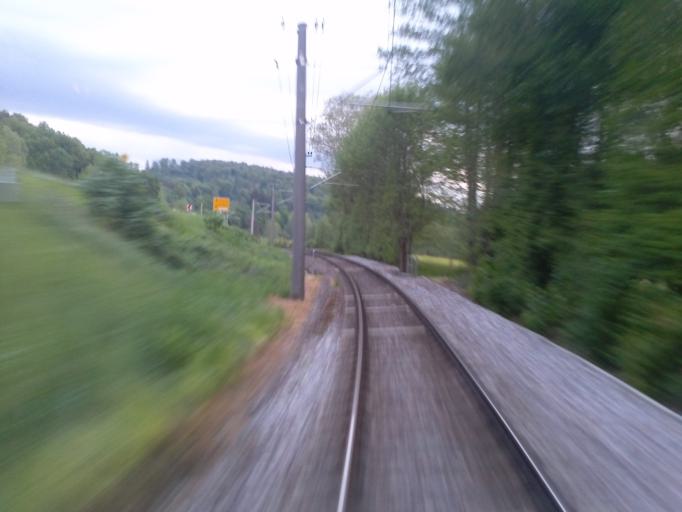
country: DE
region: Baden-Wuerttemberg
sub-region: Karlsruhe Region
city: Ettlingen
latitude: 48.8826
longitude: 8.4521
